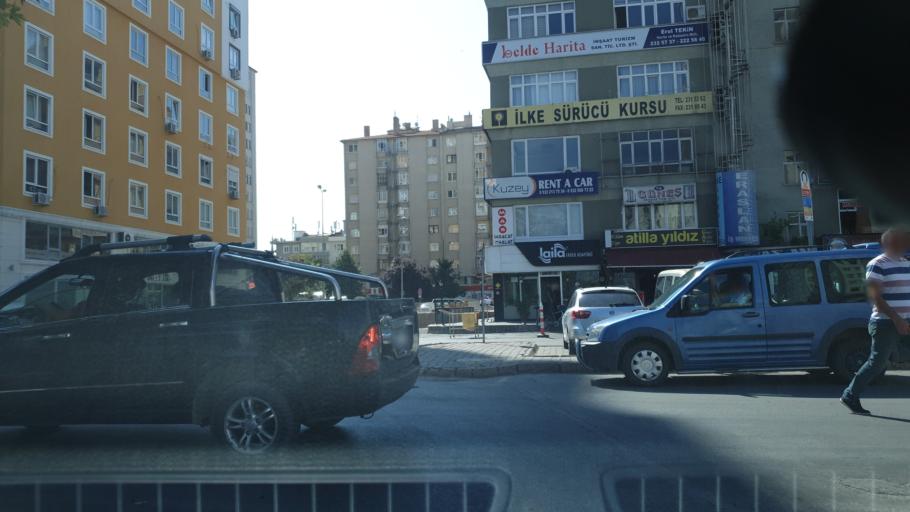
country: TR
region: Kayseri
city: Kayseri
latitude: 38.7249
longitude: 35.4923
